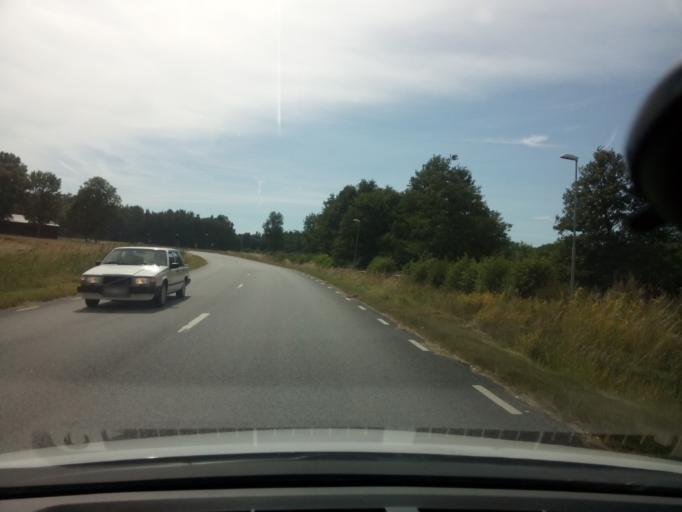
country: SE
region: Soedermanland
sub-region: Nykopings Kommun
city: Nykoping
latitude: 58.7754
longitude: 17.0735
